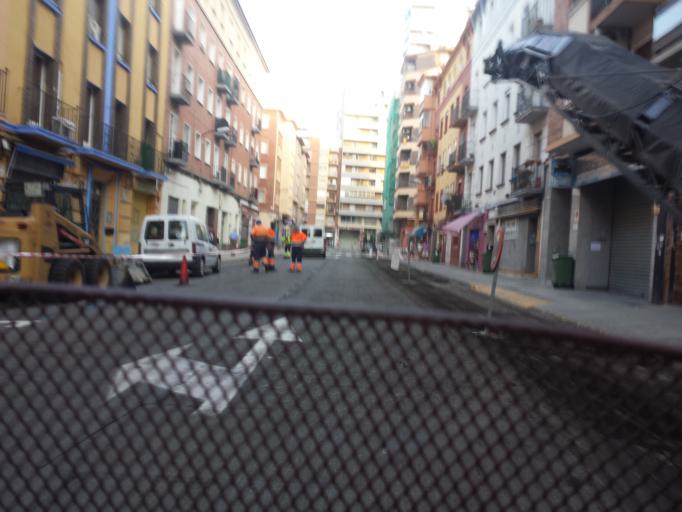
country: ES
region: Aragon
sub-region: Provincia de Zaragoza
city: Delicias
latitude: 41.6473
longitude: -0.8982
